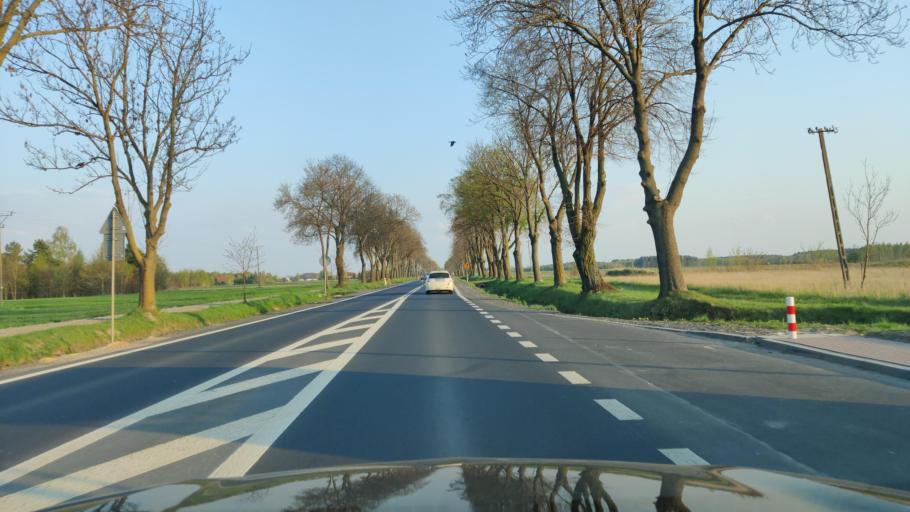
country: PL
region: Masovian Voivodeship
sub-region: Powiat pultuski
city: Zatory
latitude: 52.6153
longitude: 21.1039
